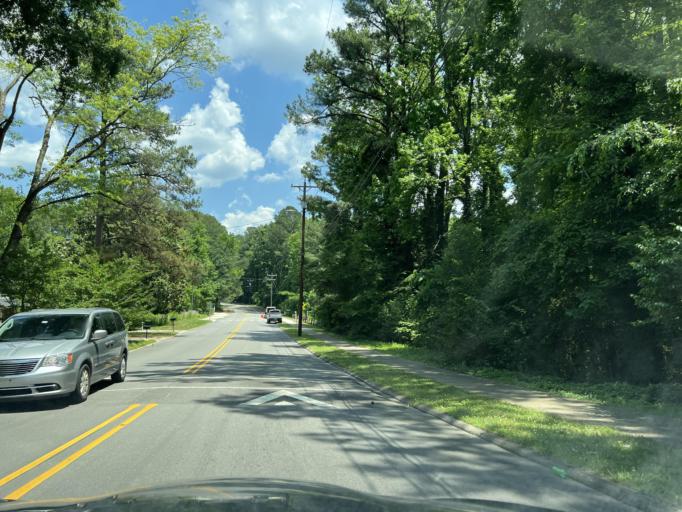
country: US
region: North Carolina
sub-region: Durham County
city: Durham
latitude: 36.0288
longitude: -78.9038
